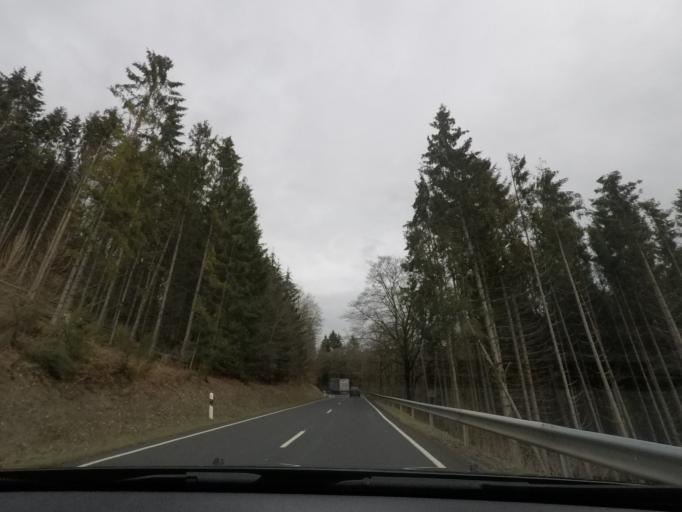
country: LU
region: Diekirch
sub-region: Canton de Wiltz
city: Winseler
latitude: 50.0008
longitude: 5.8697
